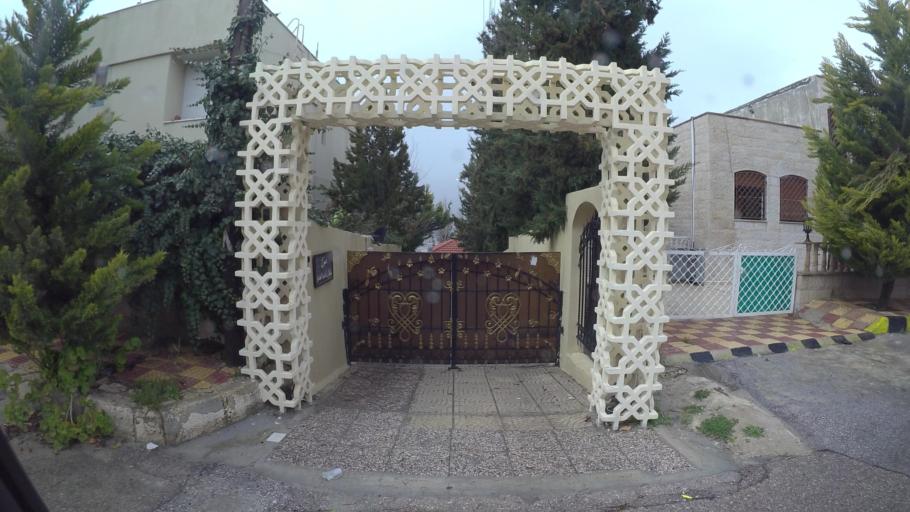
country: JO
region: Amman
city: Al Jubayhah
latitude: 32.0260
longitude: 35.8267
